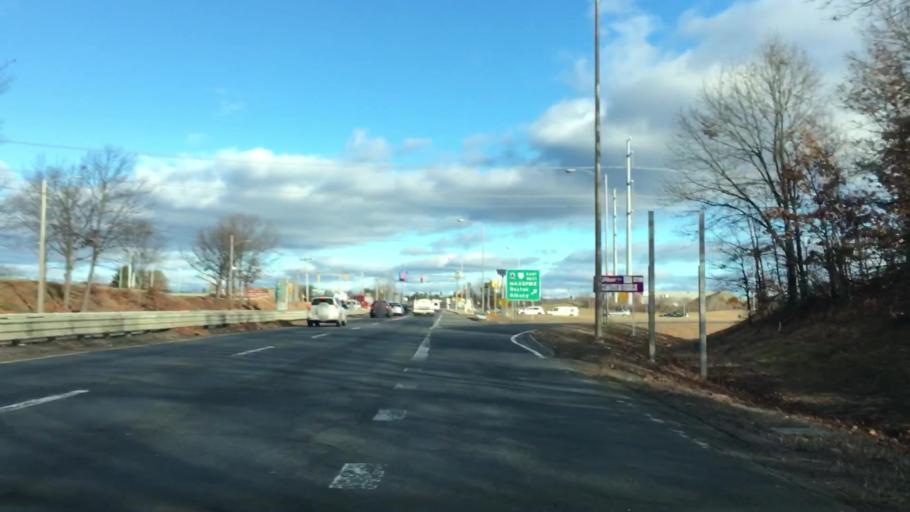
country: US
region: Massachusetts
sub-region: Hampden County
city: North Chicopee
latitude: 42.1628
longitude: -72.5470
